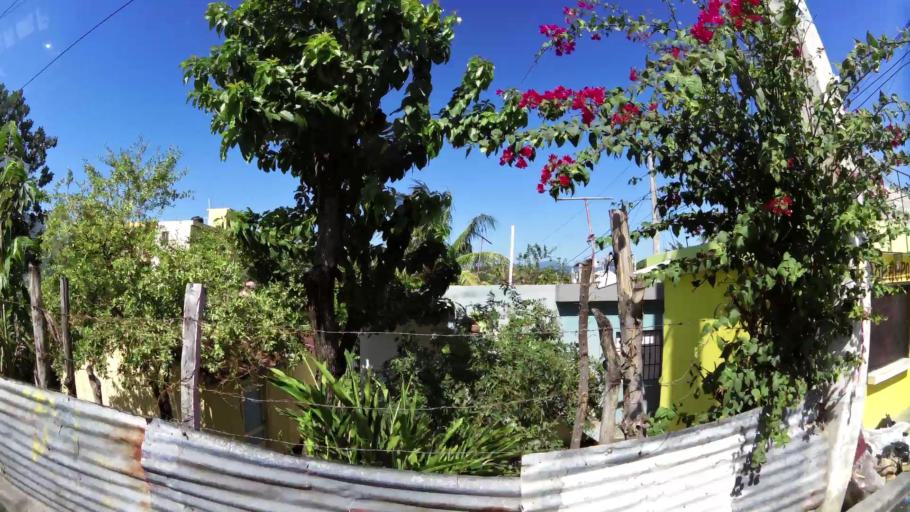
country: DO
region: San Cristobal
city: San Cristobal
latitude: 18.4266
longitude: -70.1329
